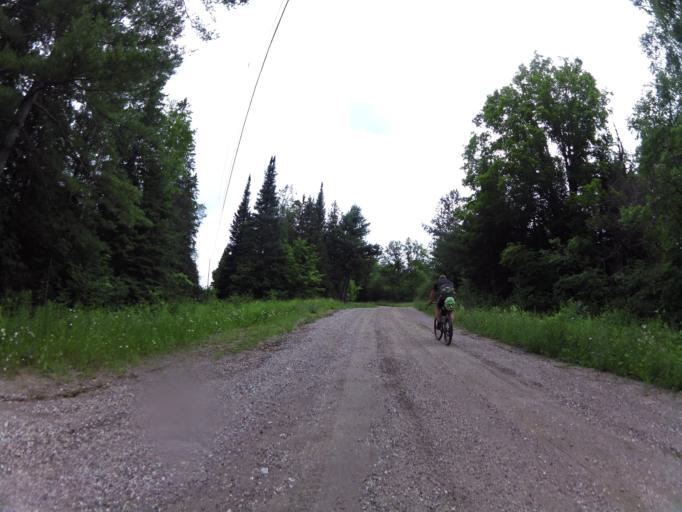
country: CA
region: Ontario
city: Renfrew
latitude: 45.0643
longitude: -76.7560
